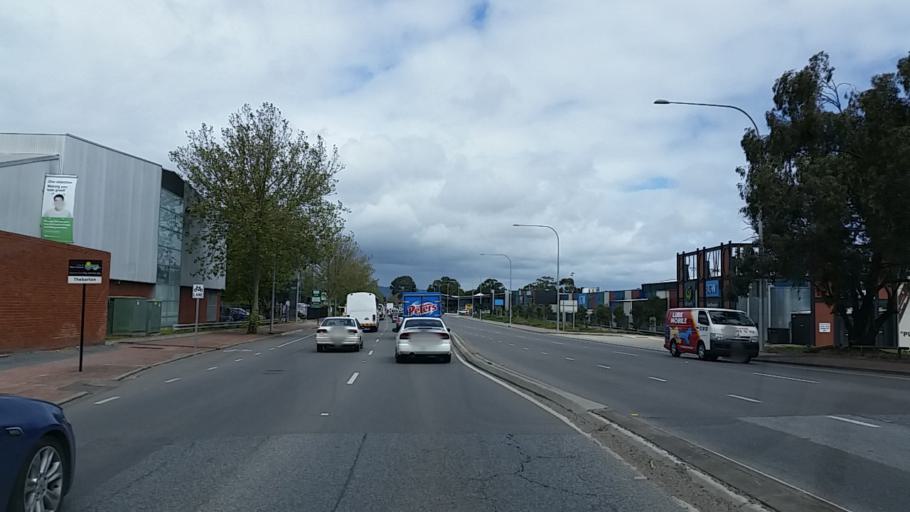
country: AU
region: South Australia
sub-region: City of West Torrens
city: Thebarton
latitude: -34.9121
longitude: 138.5646
